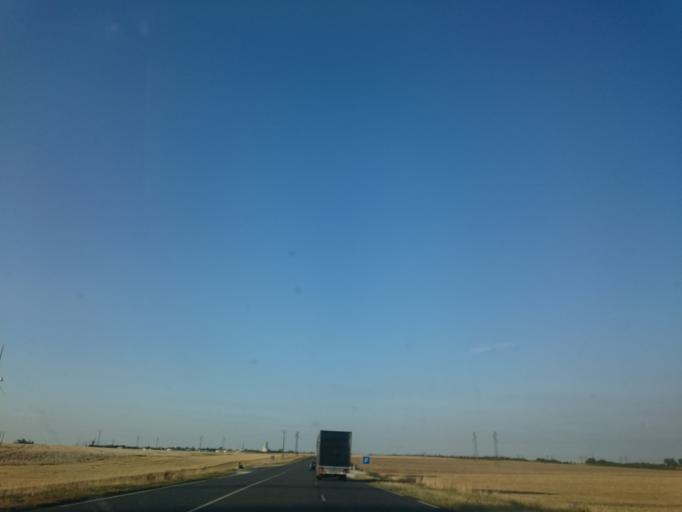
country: FR
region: Centre
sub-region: Departement d'Eure-et-Loir
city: Toury
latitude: 48.1684
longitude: 1.9186
